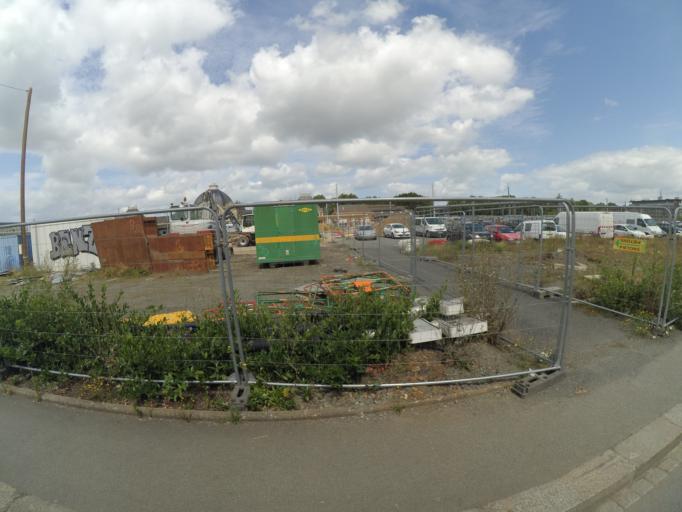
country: FR
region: Brittany
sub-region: Departement des Cotes-d'Armor
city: Saint-Brieuc
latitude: 48.5062
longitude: -2.7647
